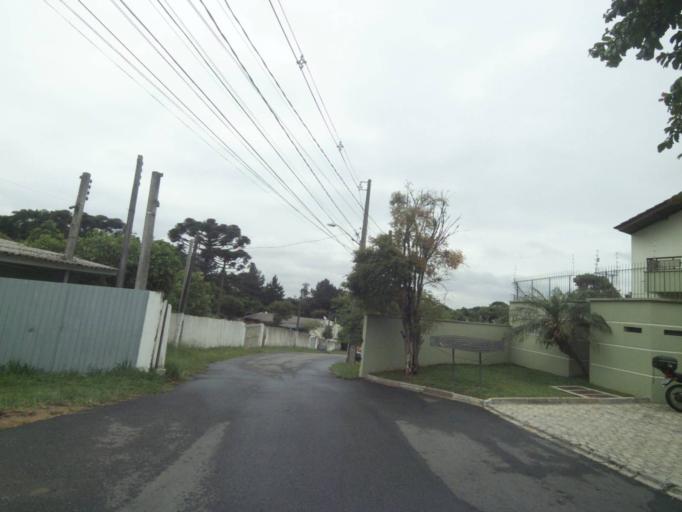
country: BR
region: Parana
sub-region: Curitiba
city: Curitiba
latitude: -25.4130
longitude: -49.2916
